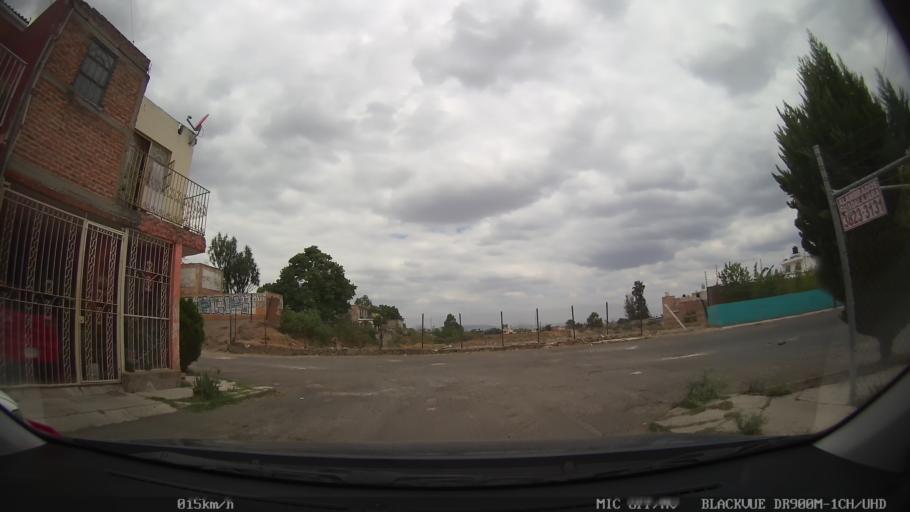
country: MX
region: Jalisco
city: Tonala
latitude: 20.6412
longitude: -103.2539
